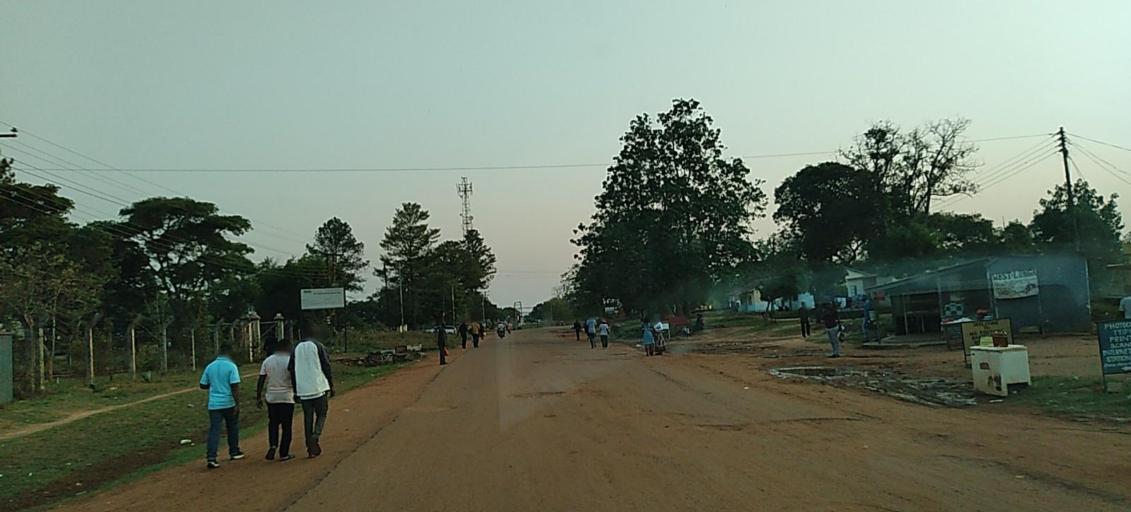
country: ZM
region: North-Western
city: Mwinilunga
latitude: -11.7370
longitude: 24.4309
